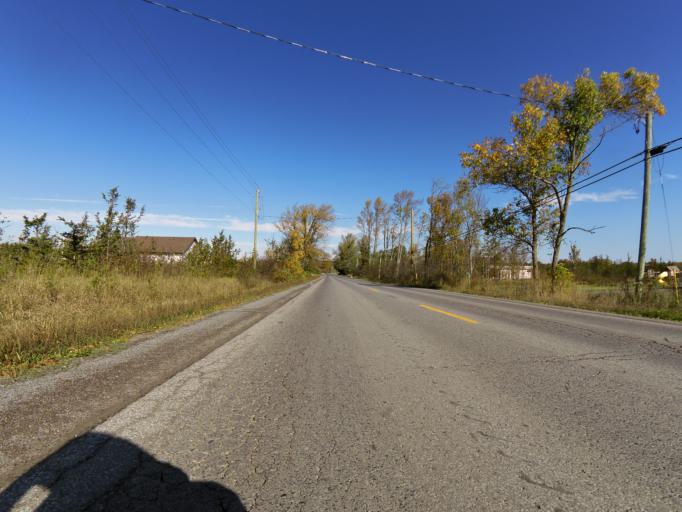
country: CA
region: Ontario
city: Prince Edward
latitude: 44.0243
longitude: -77.3663
